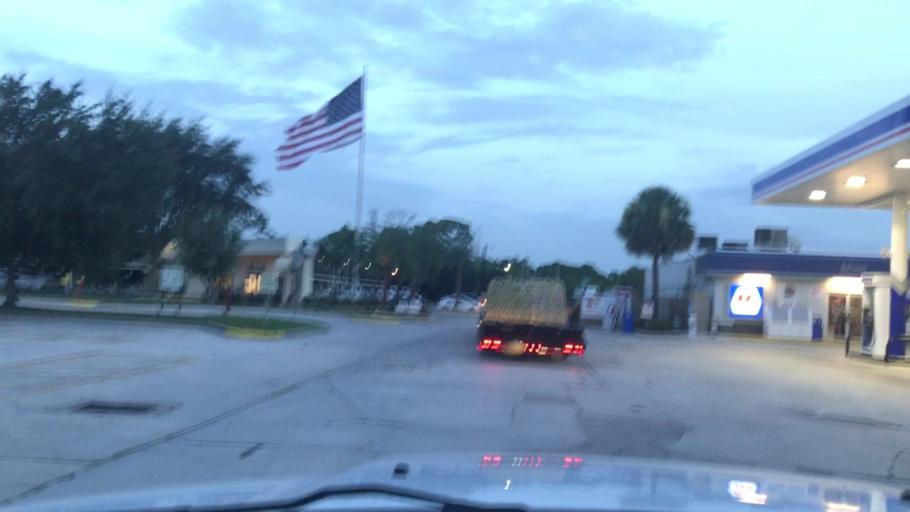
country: US
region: Florida
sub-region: Saint Lucie County
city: Fort Pierce South
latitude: 27.4127
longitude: -80.3960
